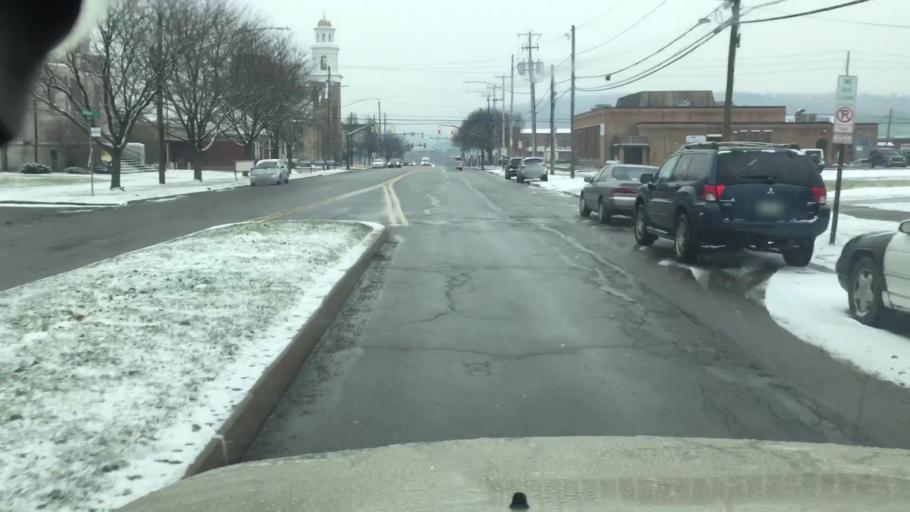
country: US
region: Pennsylvania
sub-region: Columbia County
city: Berwick
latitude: 41.0569
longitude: -76.2354
